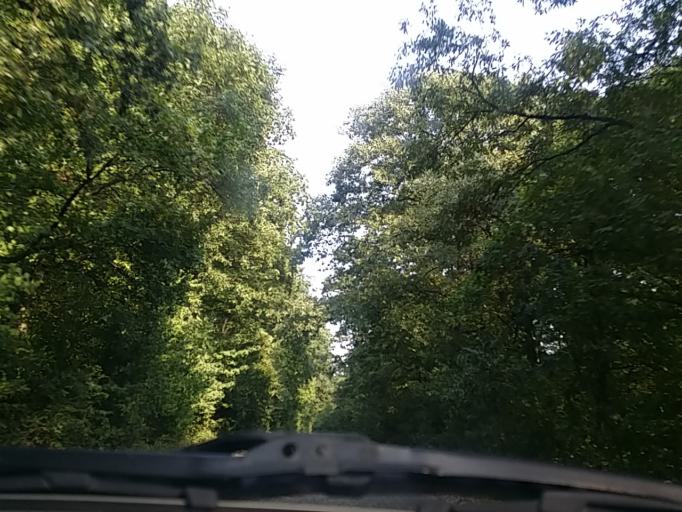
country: HU
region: Komarom-Esztergom
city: Tatabanya
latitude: 47.5297
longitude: 18.3850
